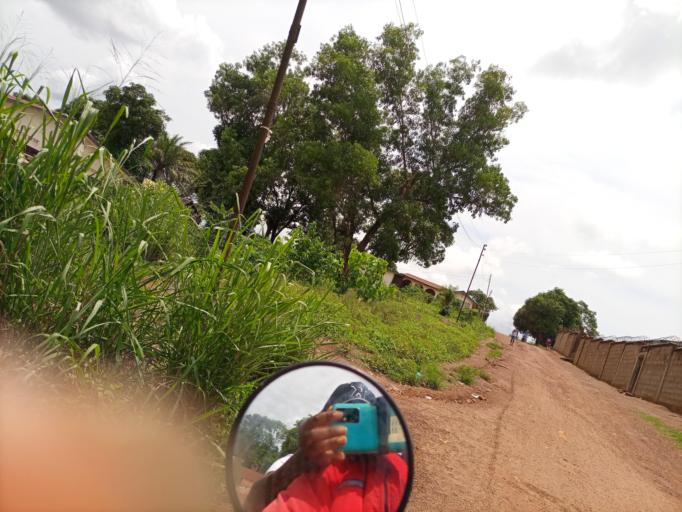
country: SL
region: Southern Province
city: Bo
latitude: 7.9704
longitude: -11.7213
